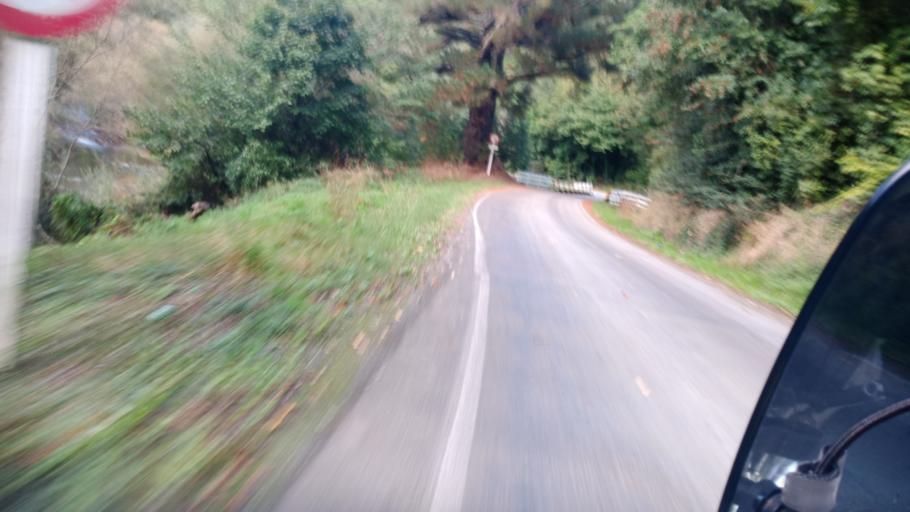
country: NZ
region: Gisborne
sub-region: Gisborne District
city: Gisborne
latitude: -38.5324
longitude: 177.5340
